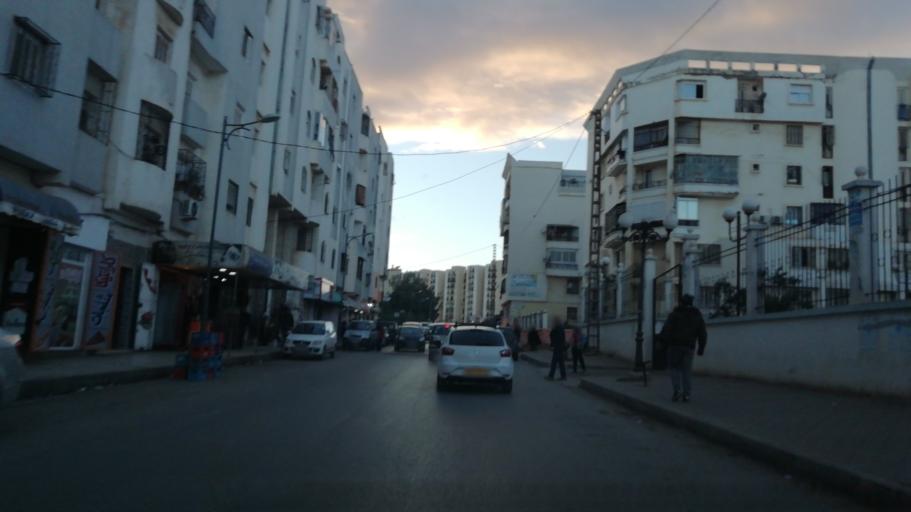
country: DZ
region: Oran
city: Bir el Djir
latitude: 35.6986
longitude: -0.5662
